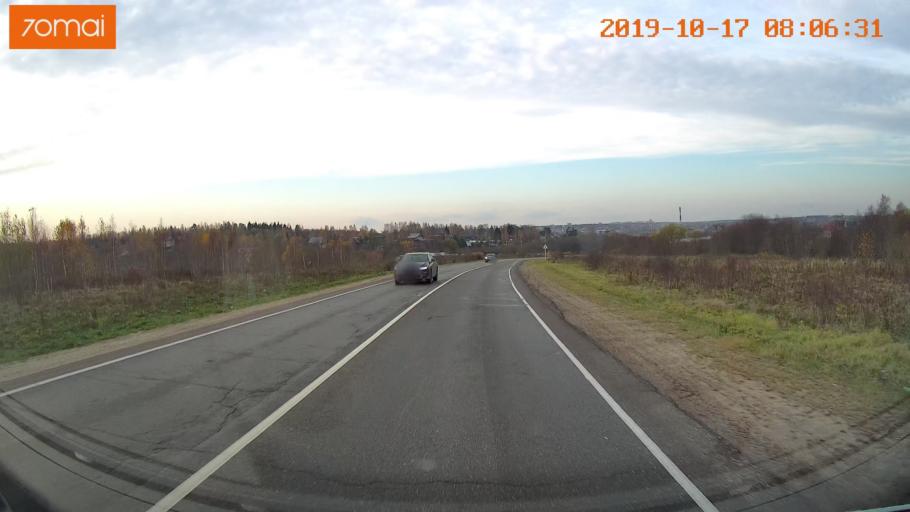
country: RU
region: Vladimir
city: Belaya Rechka
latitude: 56.3218
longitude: 39.4129
